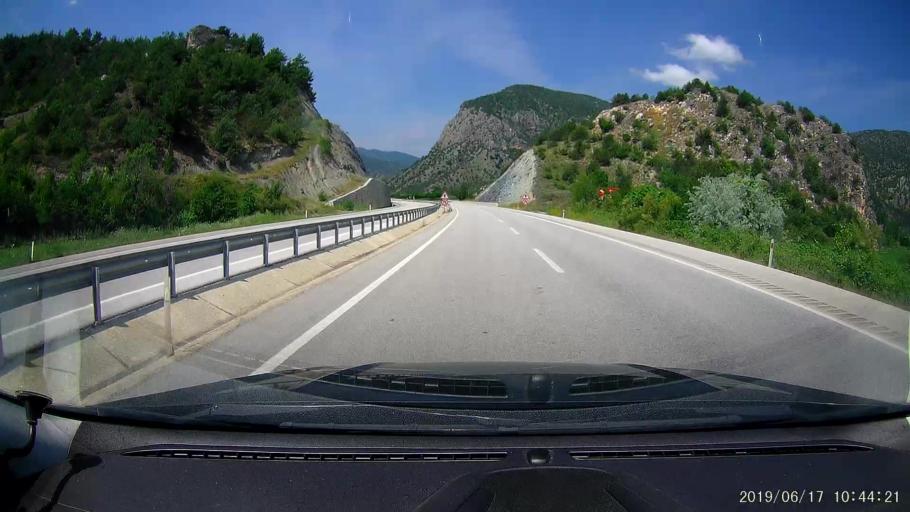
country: TR
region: Corum
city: Hacihamza
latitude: 41.0725
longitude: 34.5144
